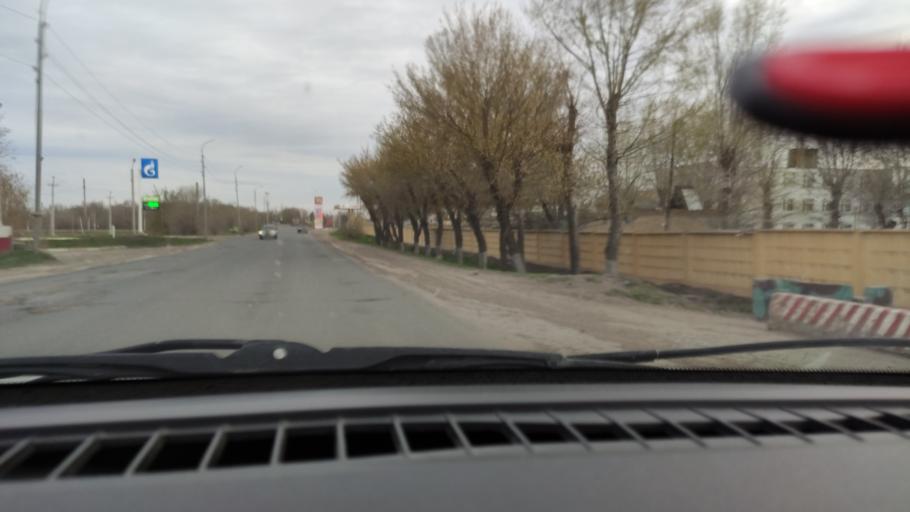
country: RU
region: Orenburg
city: Tatarskaya Kargala
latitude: 51.8804
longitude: 55.1503
